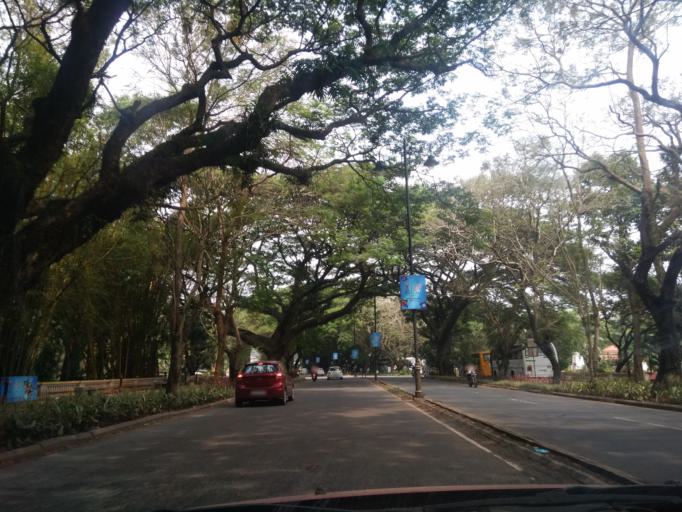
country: IN
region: Goa
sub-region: North Goa
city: Panaji
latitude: 15.4953
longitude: 73.8188
